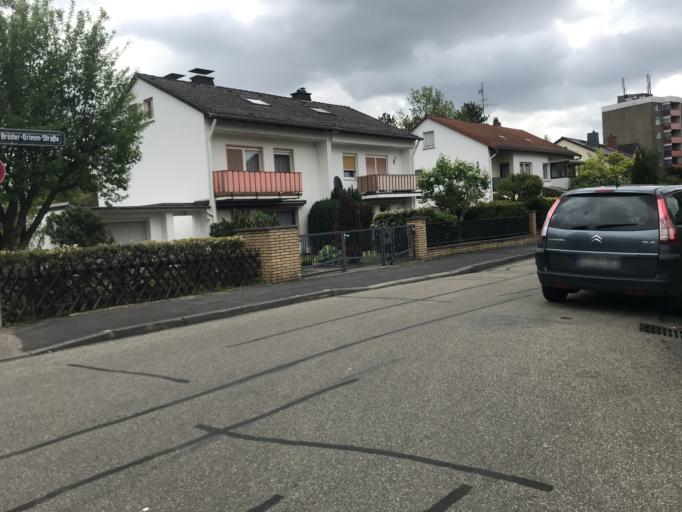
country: DE
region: Hesse
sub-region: Regierungsbezirk Darmstadt
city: Walluf
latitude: 50.0721
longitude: 8.1812
